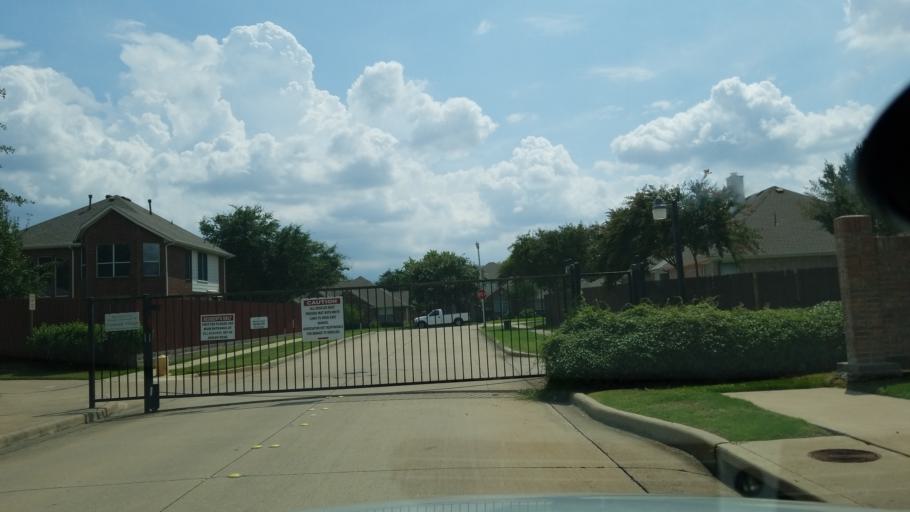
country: US
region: Texas
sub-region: Dallas County
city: Garland
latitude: 32.9294
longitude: -96.6604
